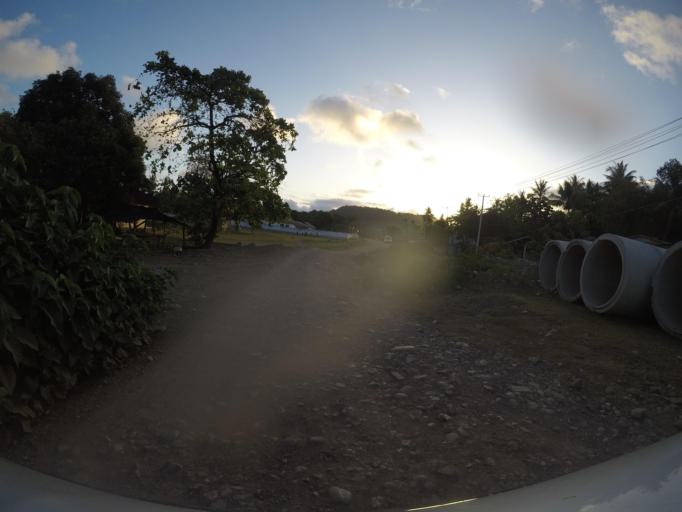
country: TL
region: Baucau
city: Venilale
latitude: -8.7497
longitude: 126.6997
